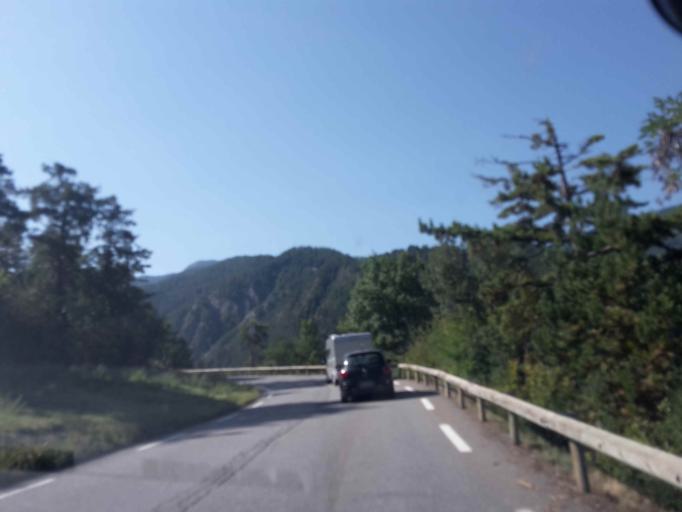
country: FR
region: Provence-Alpes-Cote d'Azur
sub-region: Departement des Hautes-Alpes
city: Guillestre
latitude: 44.6513
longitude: 6.6506
